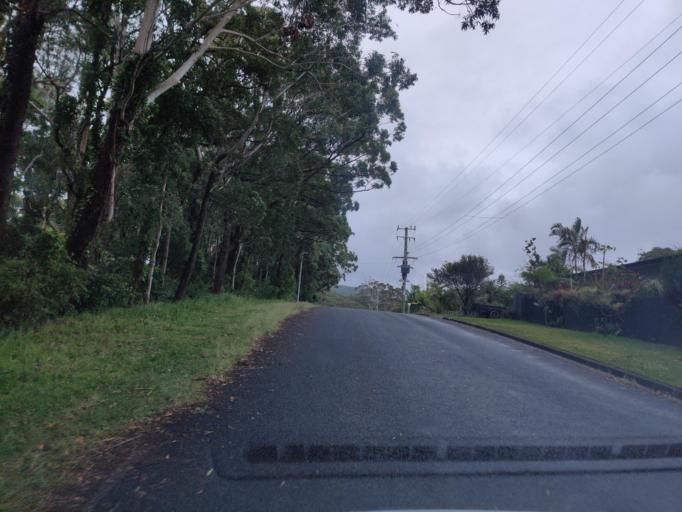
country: AU
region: New South Wales
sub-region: Great Lakes
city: Forster
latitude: -32.3832
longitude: 152.5036
